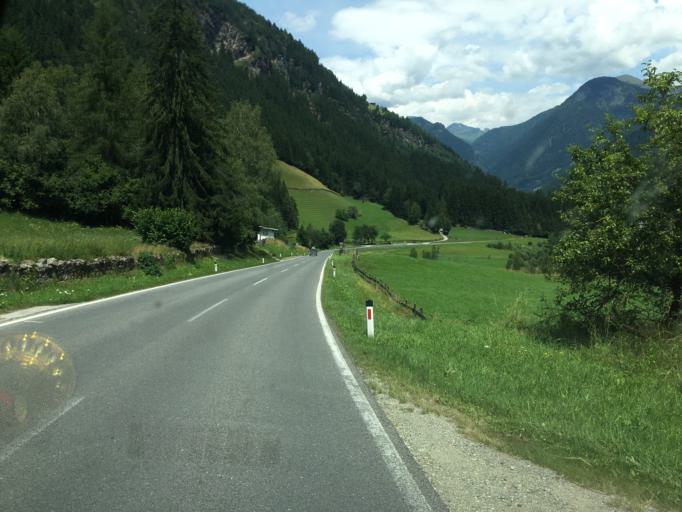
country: AT
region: Carinthia
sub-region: Politischer Bezirk Spittal an der Drau
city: Winklern
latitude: 46.8789
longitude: 12.8802
